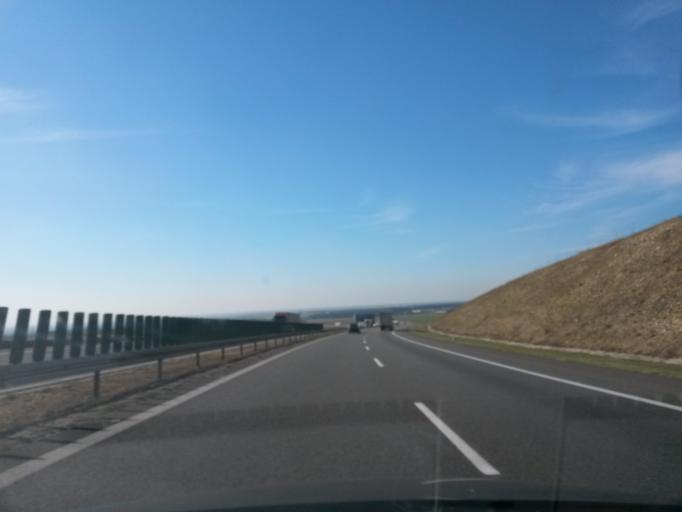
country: PL
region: Opole Voivodeship
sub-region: Powiat krapkowicki
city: Rozwadza
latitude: 50.4803
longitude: 18.1231
